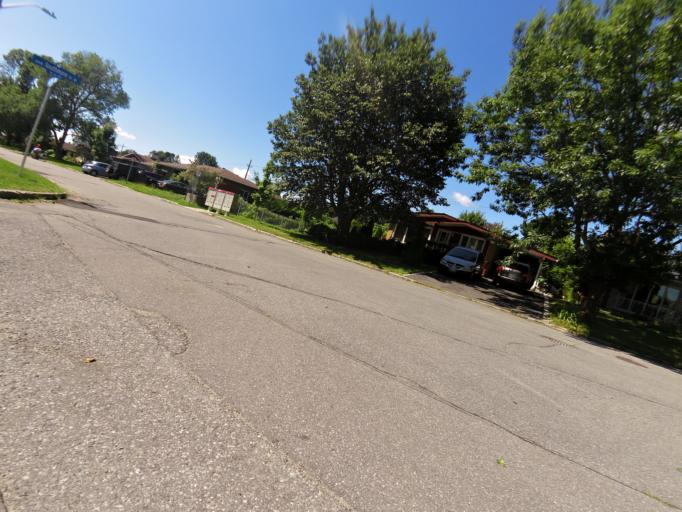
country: CA
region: Ontario
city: Ottawa
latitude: 45.3586
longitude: -75.6837
